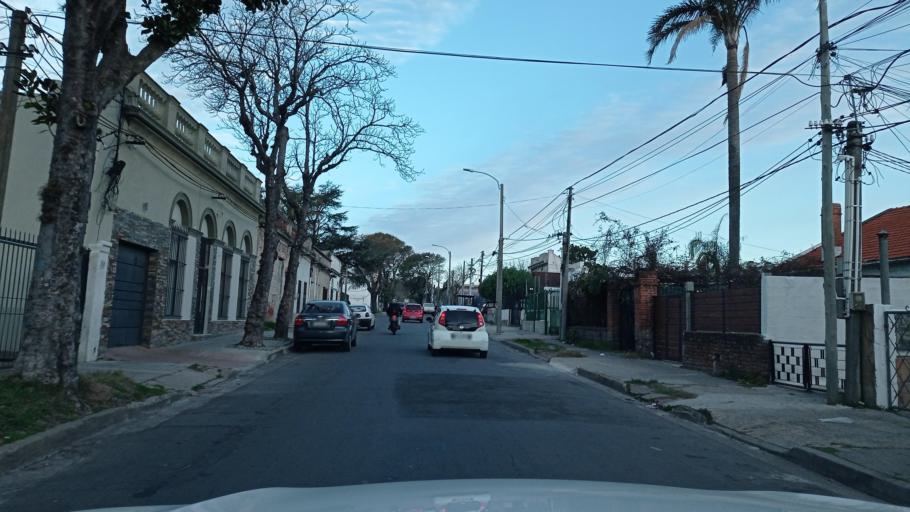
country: UY
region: Montevideo
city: Montevideo
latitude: -34.8701
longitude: -56.1448
